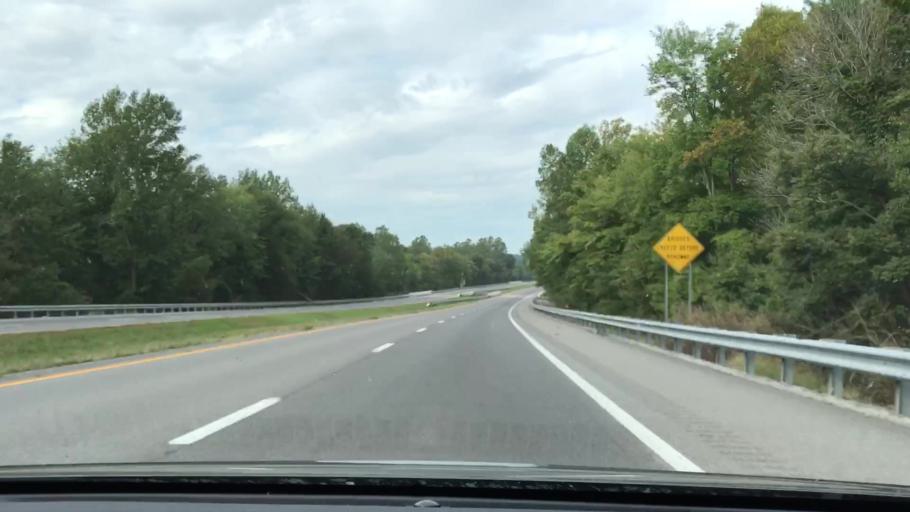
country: US
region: Kentucky
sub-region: Graves County
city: Mayfield
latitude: 36.7907
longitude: -88.5215
